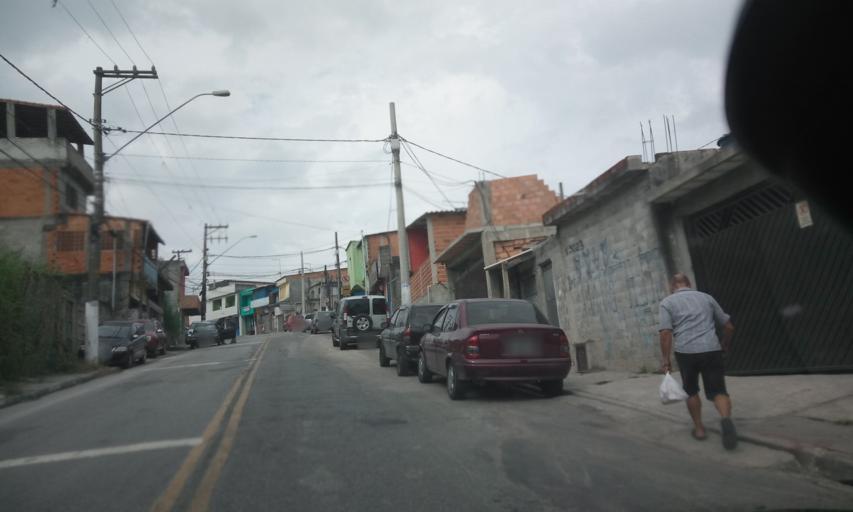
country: BR
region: Sao Paulo
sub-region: Sao Bernardo Do Campo
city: Sao Bernardo do Campo
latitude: -23.7717
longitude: -46.6010
